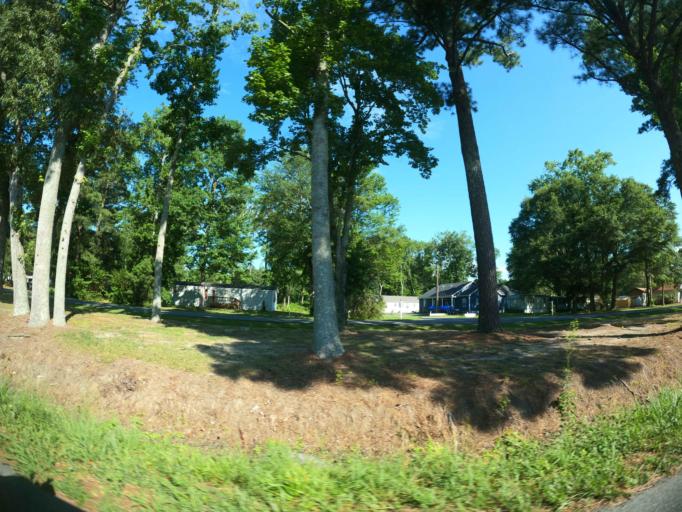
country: US
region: Delaware
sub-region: Sussex County
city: Ocean View
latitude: 38.5156
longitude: -75.1009
